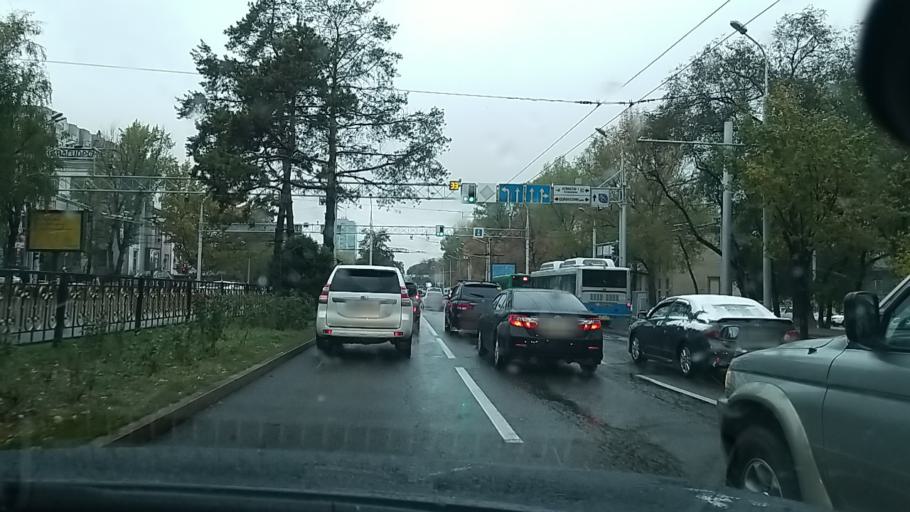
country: KZ
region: Almaty Qalasy
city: Almaty
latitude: 43.2416
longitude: 76.9352
